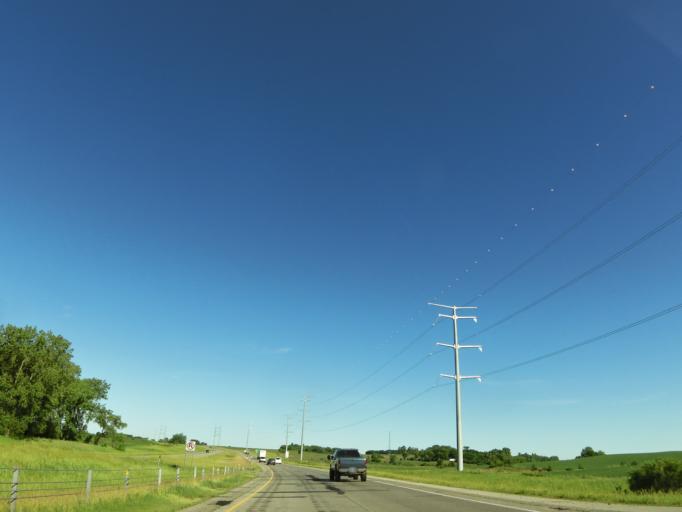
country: US
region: Minnesota
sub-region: Grant County
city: Elbow Lake
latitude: 46.0041
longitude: -95.7361
